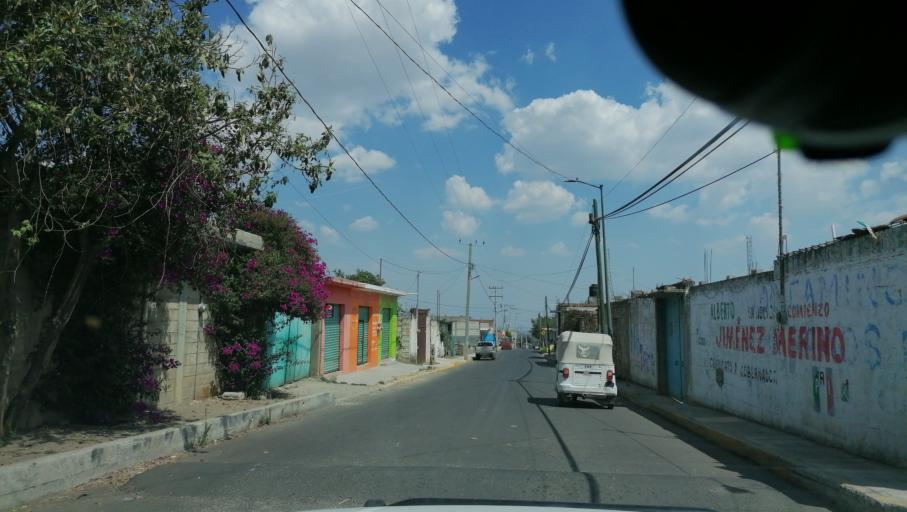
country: MX
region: Puebla
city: San Andres Calpan
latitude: 19.1039
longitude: -98.4769
